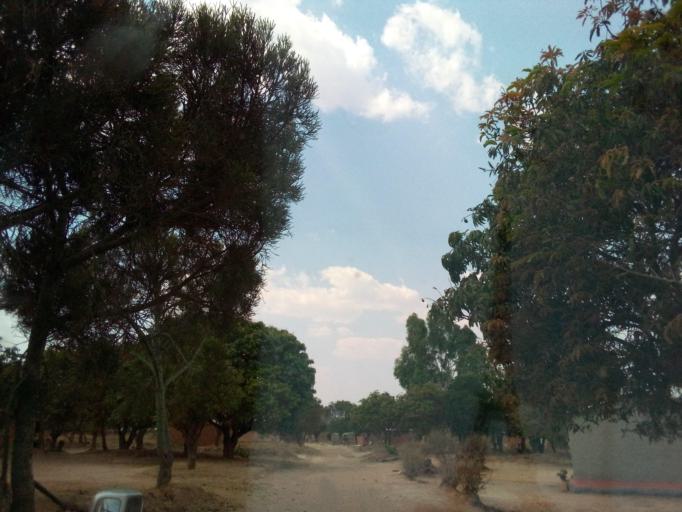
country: ZM
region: Northern
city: Mpika
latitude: -11.8351
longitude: 31.3877
